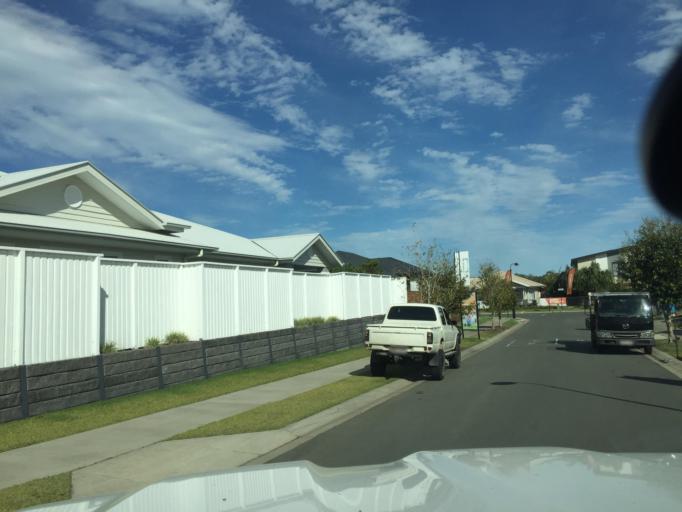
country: AU
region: Queensland
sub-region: Moreton Bay
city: Morayfield
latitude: -27.1229
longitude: 152.9959
